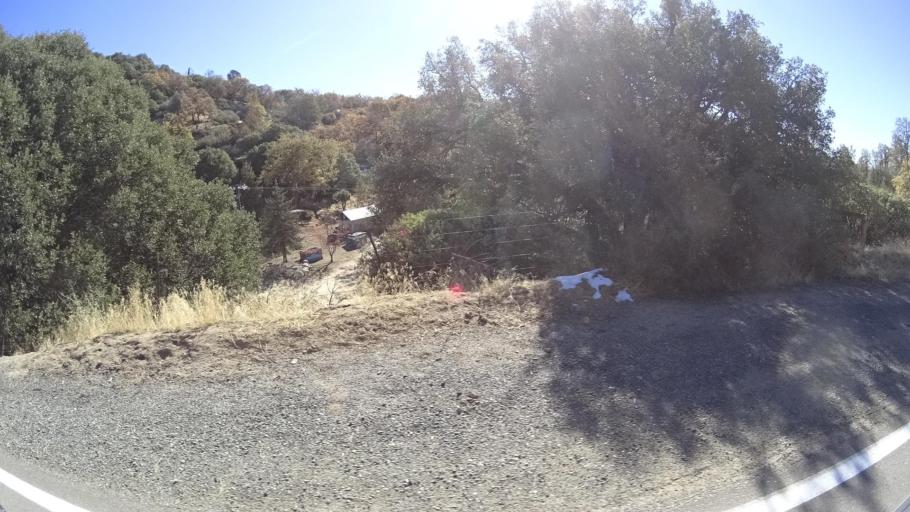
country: US
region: California
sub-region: Kern County
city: Alta Sierra
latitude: 35.7398
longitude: -118.6217
